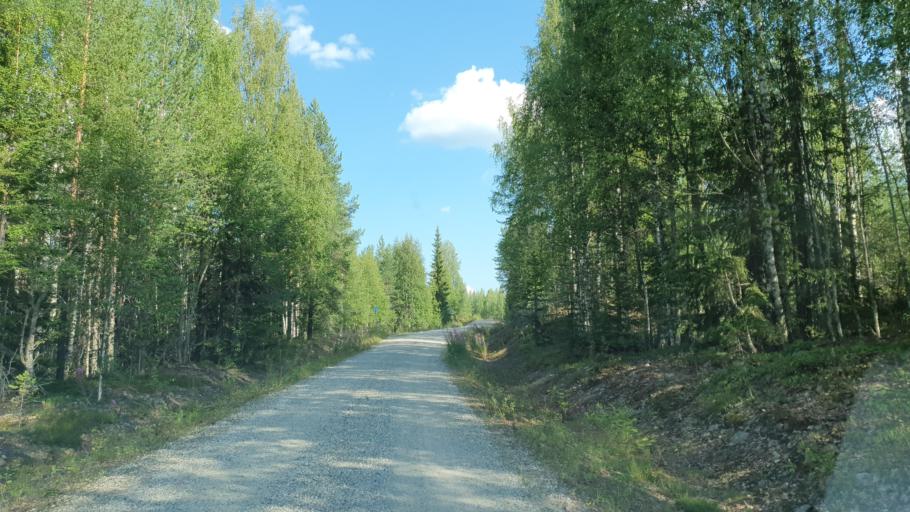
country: FI
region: Kainuu
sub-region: Kehys-Kainuu
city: Kuhmo
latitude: 63.9529
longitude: 29.5620
